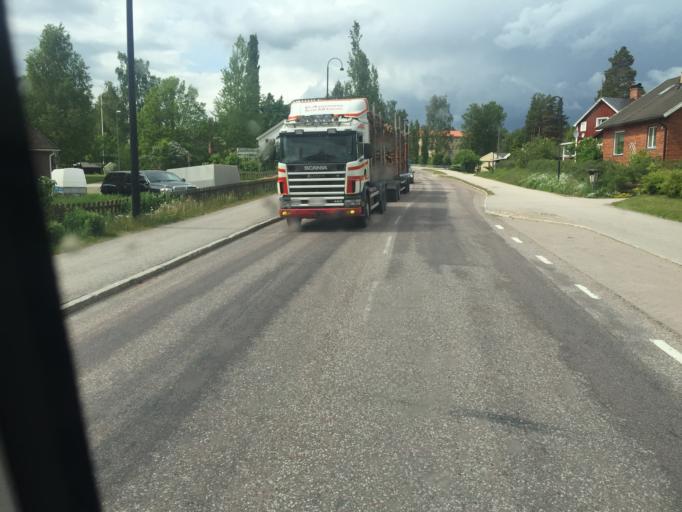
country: SE
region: Dalarna
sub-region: Vansbro Kommun
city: Vansbro
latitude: 60.5092
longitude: 14.2232
